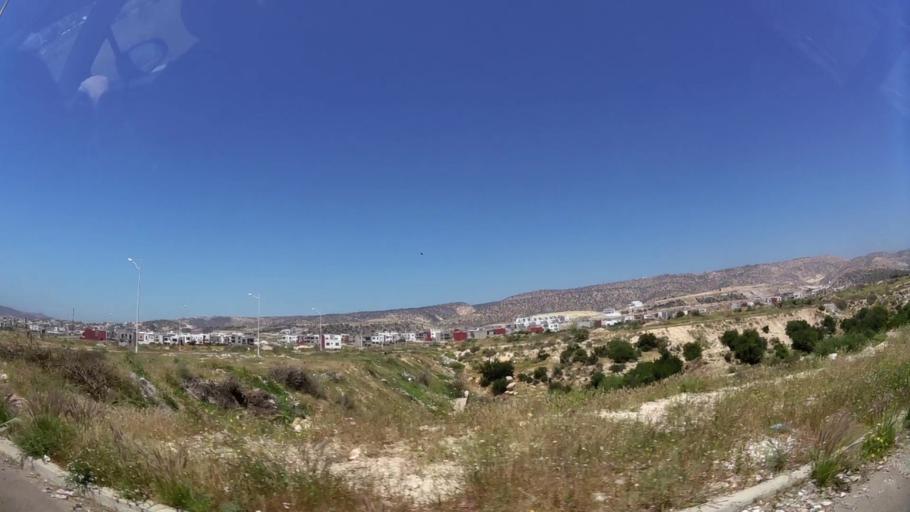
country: MA
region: Oued ed Dahab-Lagouira
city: Dakhla
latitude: 30.4381
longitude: -9.5696
